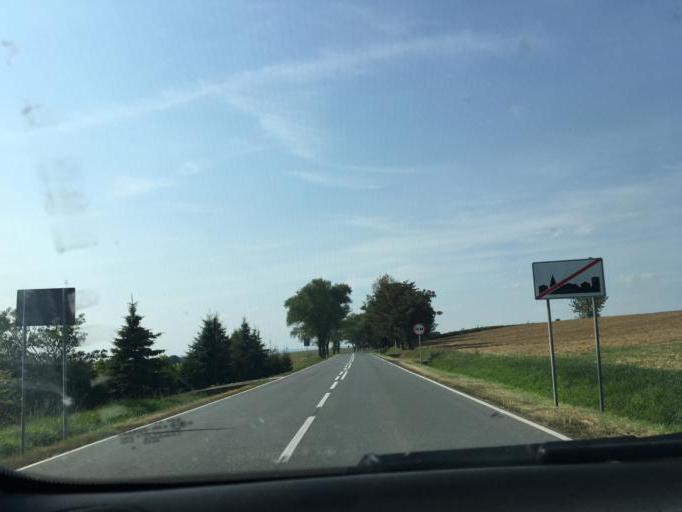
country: PL
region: Opole Voivodeship
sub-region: Powiat nyski
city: Nysa
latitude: 50.4264
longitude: 17.4288
